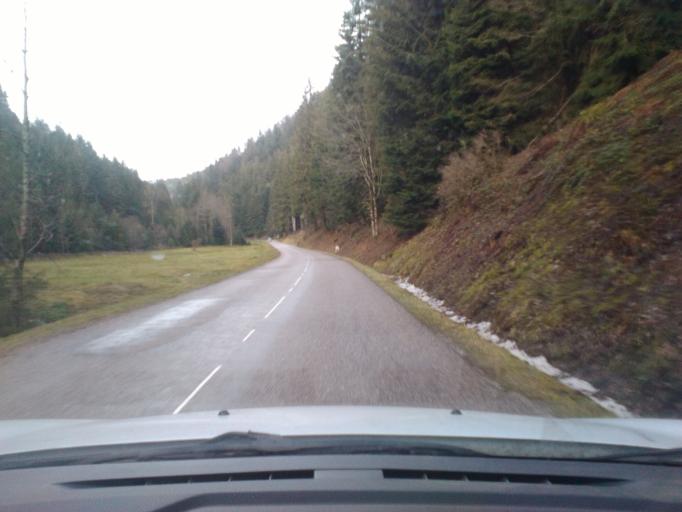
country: FR
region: Lorraine
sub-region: Departement des Vosges
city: Xonrupt-Longemer
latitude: 48.1015
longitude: 6.9752
